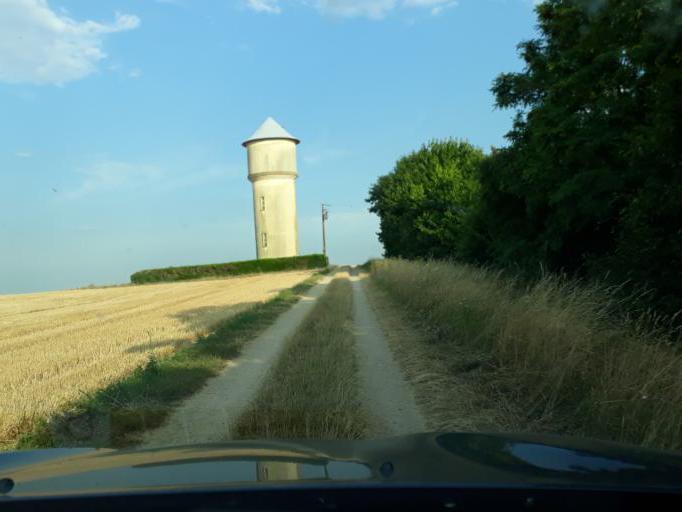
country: FR
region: Centre
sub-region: Departement du Loir-et-Cher
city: Ouzouer-le-Marche
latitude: 47.8149
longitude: 1.4960
